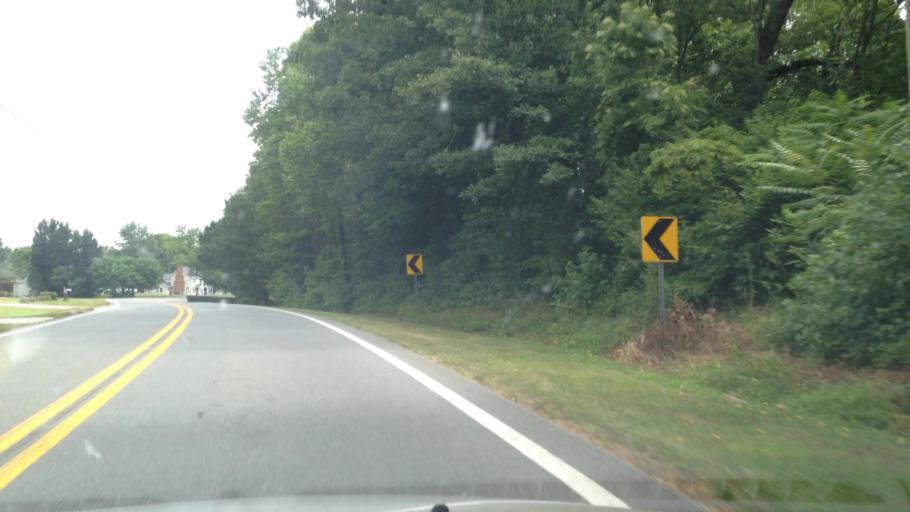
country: US
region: North Carolina
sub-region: Rockingham County
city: Reidsville
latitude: 36.4049
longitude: -79.6205
